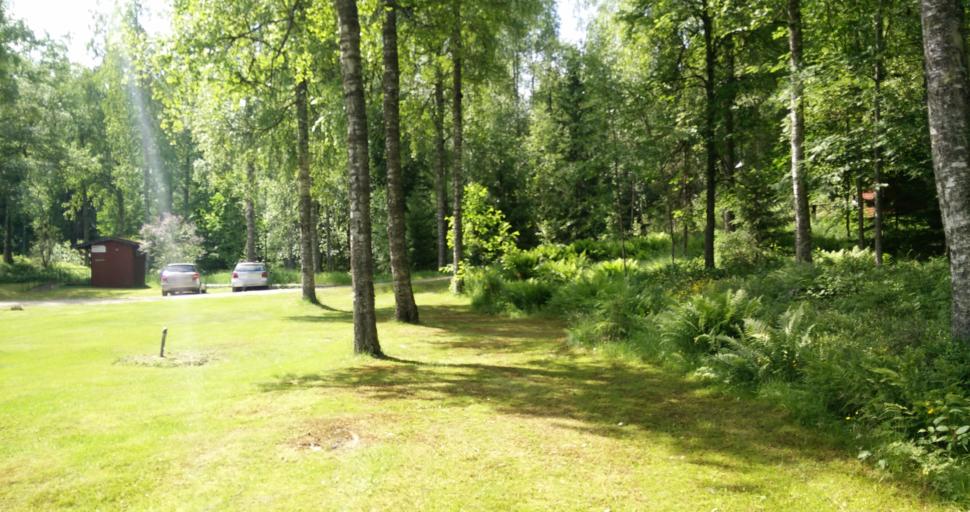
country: SE
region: Vaermland
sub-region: Hagfors Kommun
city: Hagfors
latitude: 59.9945
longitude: 13.5673
